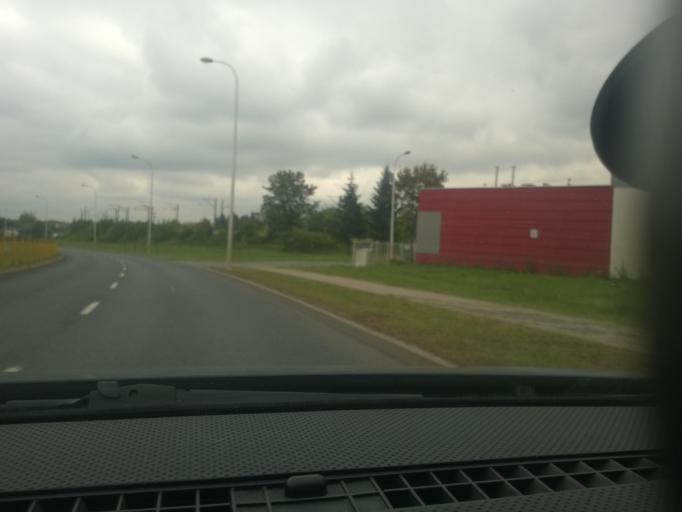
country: PL
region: Greater Poland Voivodeship
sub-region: Kalisz
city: Kalisz
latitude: 51.7447
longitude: 18.0739
